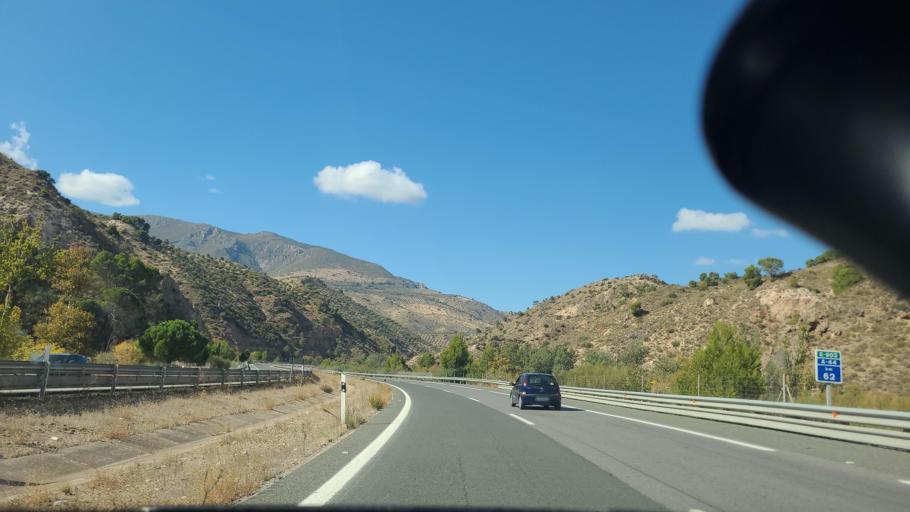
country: ES
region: Andalusia
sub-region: Provincia de Jaen
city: Cambil
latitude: 37.6575
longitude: -3.6068
